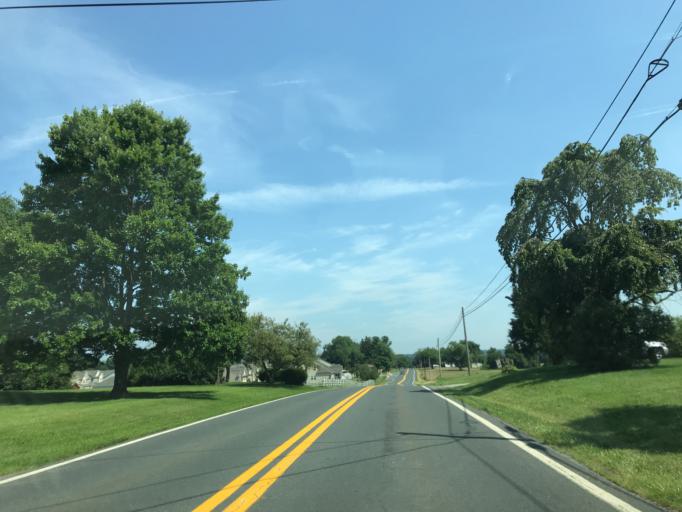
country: US
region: Maryland
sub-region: Carroll County
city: Taneytown
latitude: 39.6400
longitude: -77.1604
